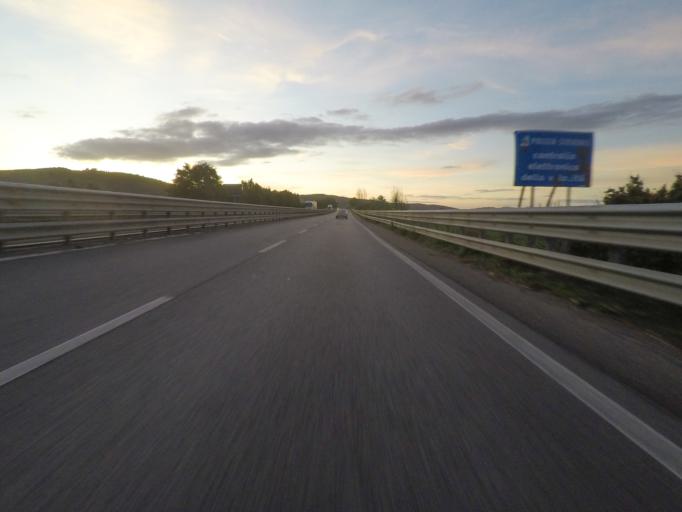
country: IT
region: Tuscany
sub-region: Provincia di Siena
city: Sinalunga
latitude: 43.2234
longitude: 11.7490
